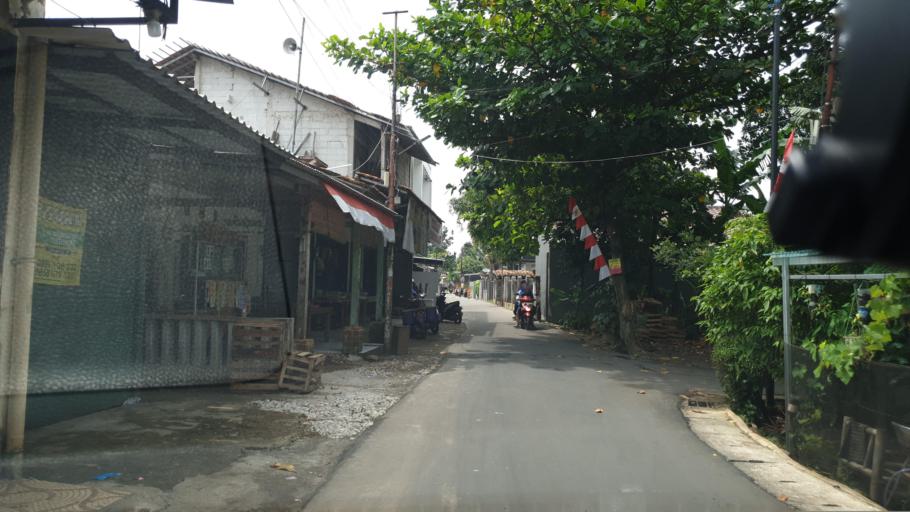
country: ID
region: West Java
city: Sawangan
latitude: -6.3730
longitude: 106.7609
